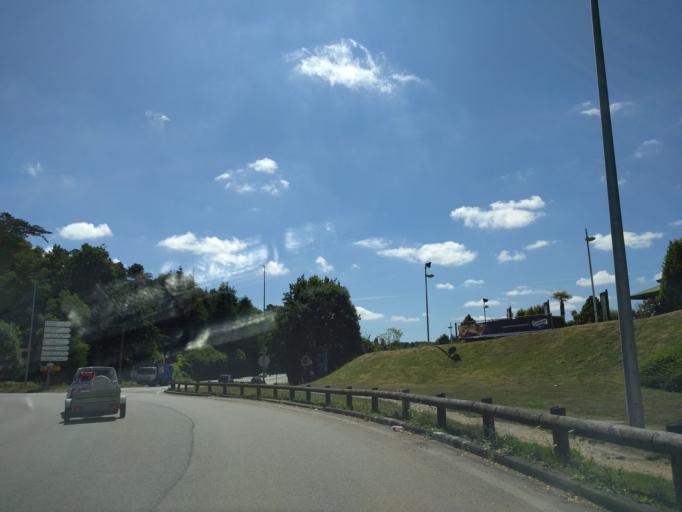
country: FR
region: Brittany
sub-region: Departement du Finistere
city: Quimper
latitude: 47.9790
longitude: -4.0952
